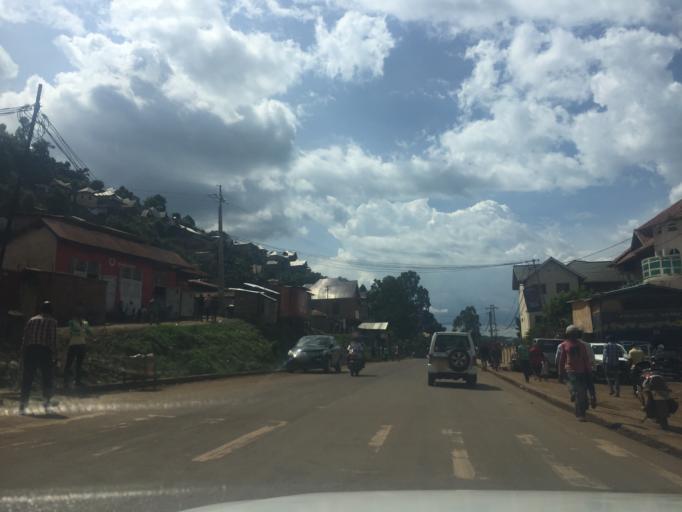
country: CD
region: South Kivu
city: Bukavu
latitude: -2.4883
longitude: 28.8473
